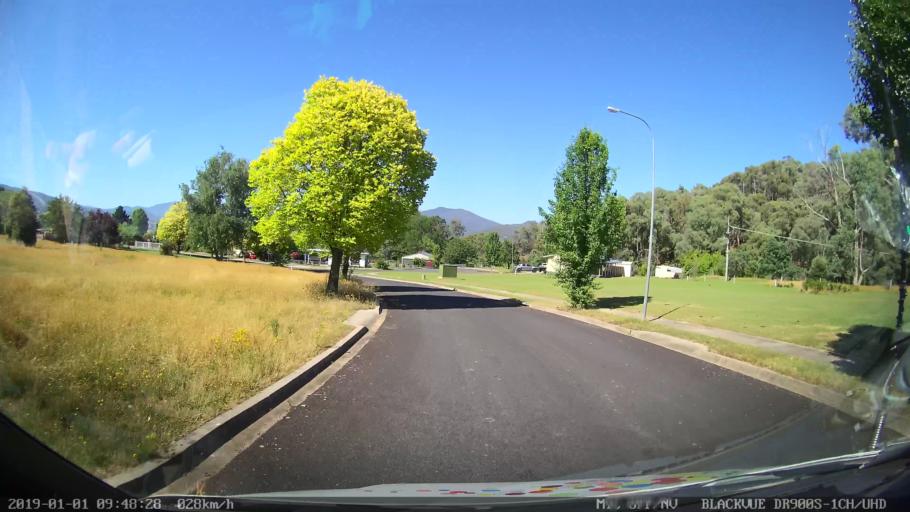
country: AU
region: New South Wales
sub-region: Snowy River
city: Jindabyne
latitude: -36.2120
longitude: 148.1322
